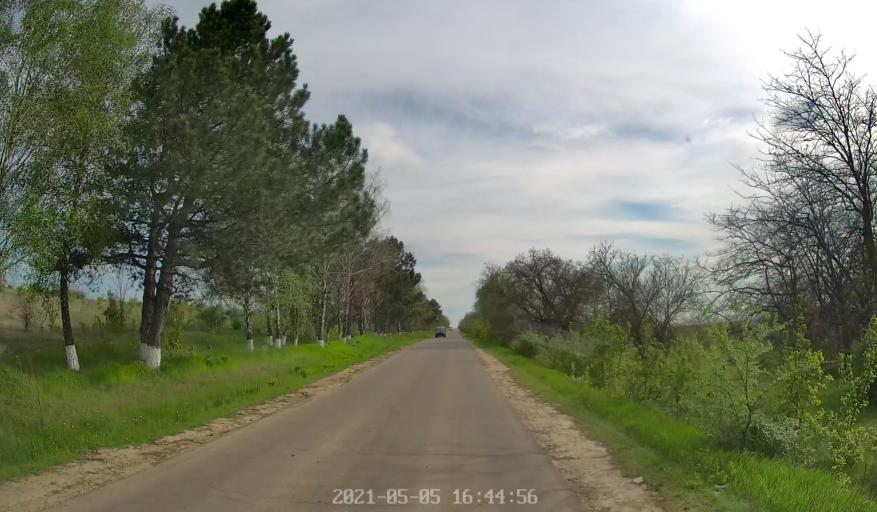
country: MD
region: Criuleni
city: Criuleni
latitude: 47.1141
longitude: 29.1943
